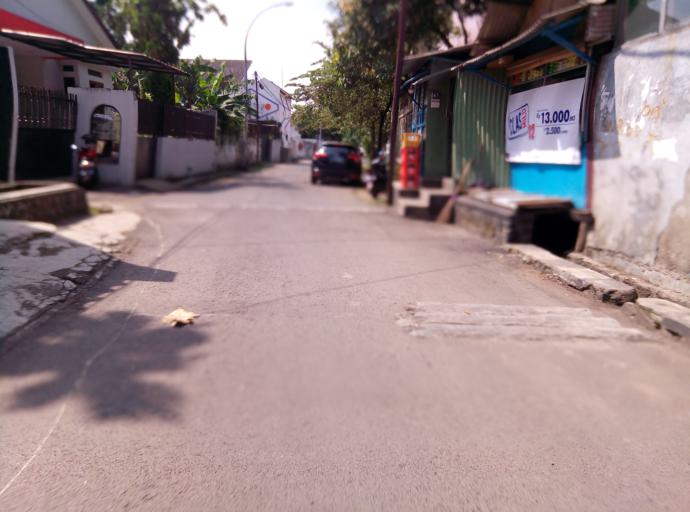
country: ID
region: West Java
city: Bandung
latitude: -6.9437
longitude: 107.6449
